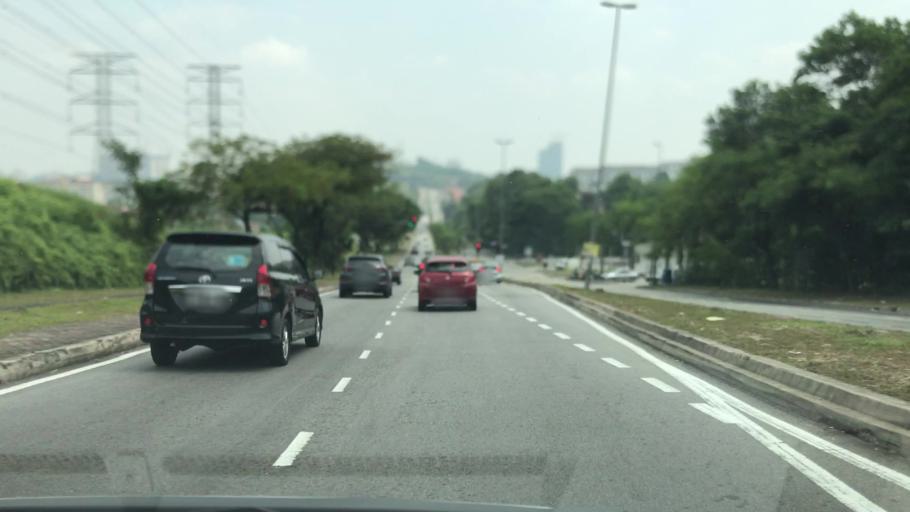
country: MY
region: Selangor
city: Kampong Baharu Balakong
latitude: 3.0297
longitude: 101.6807
